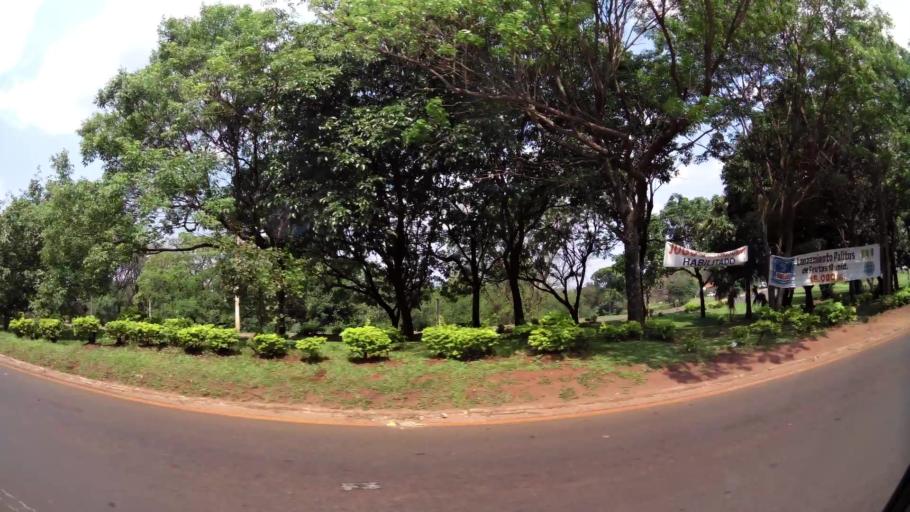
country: PY
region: Alto Parana
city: Presidente Franco
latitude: -25.5151
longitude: -54.6421
